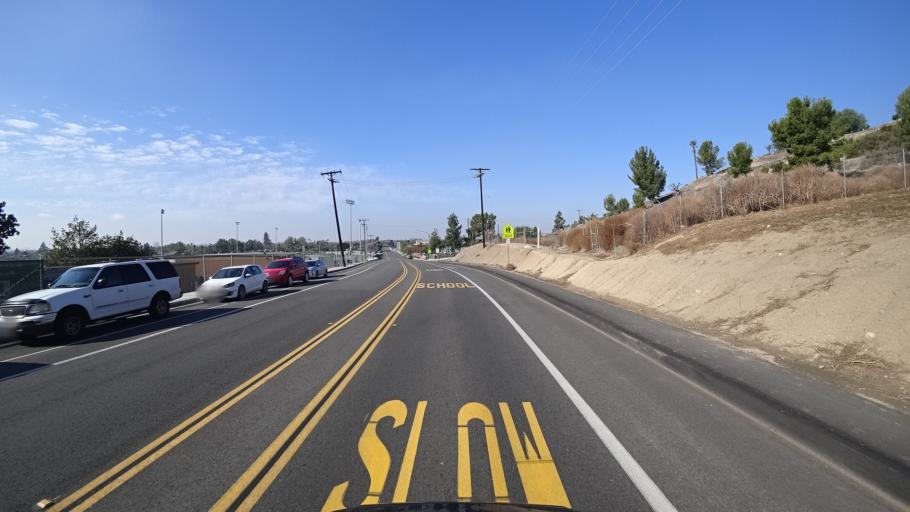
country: US
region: California
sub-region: Orange County
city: North Tustin
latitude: 33.7689
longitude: -117.7982
